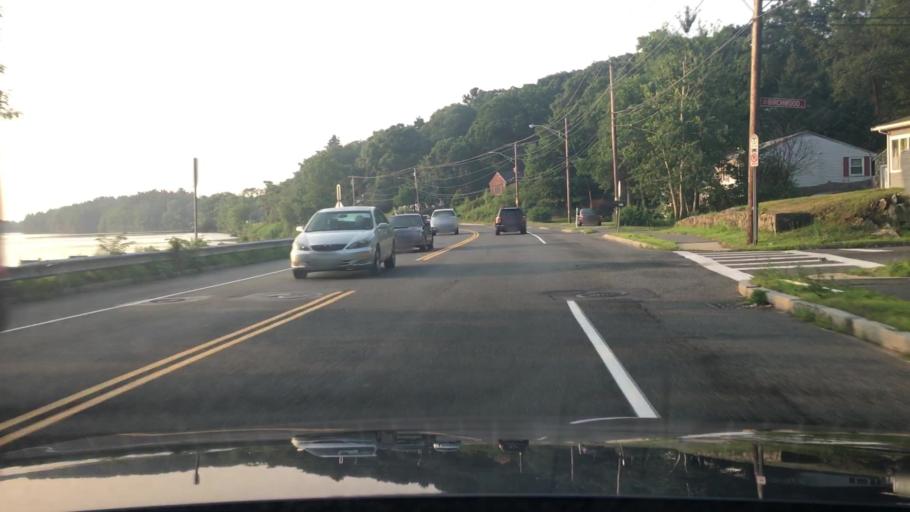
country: US
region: Massachusetts
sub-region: Essex County
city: Saugus
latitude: 42.4816
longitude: -71.0082
